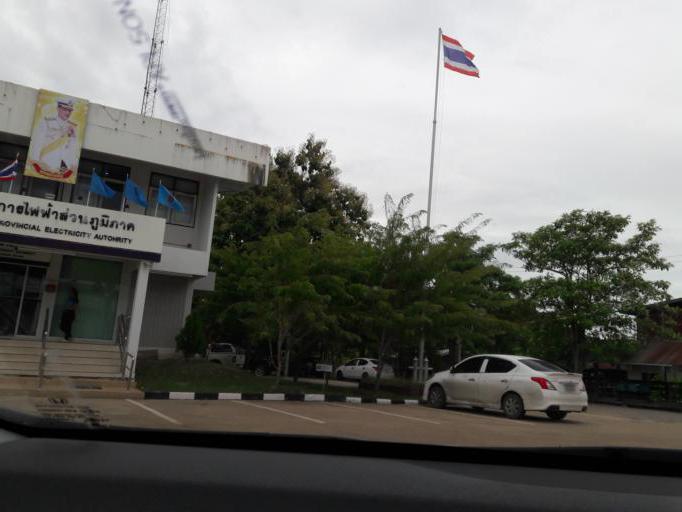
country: TH
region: Samut Sakhon
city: Ban Phaeo
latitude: 13.5495
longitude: 100.0405
